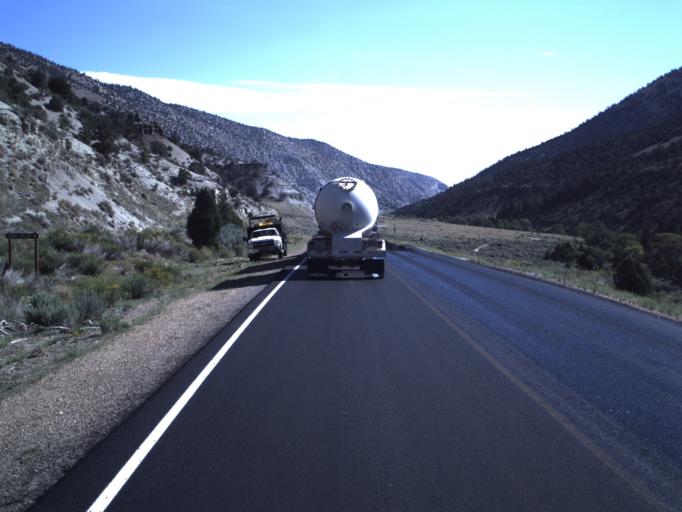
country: US
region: Utah
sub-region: Carbon County
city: Helper
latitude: 39.9359
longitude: -110.6695
